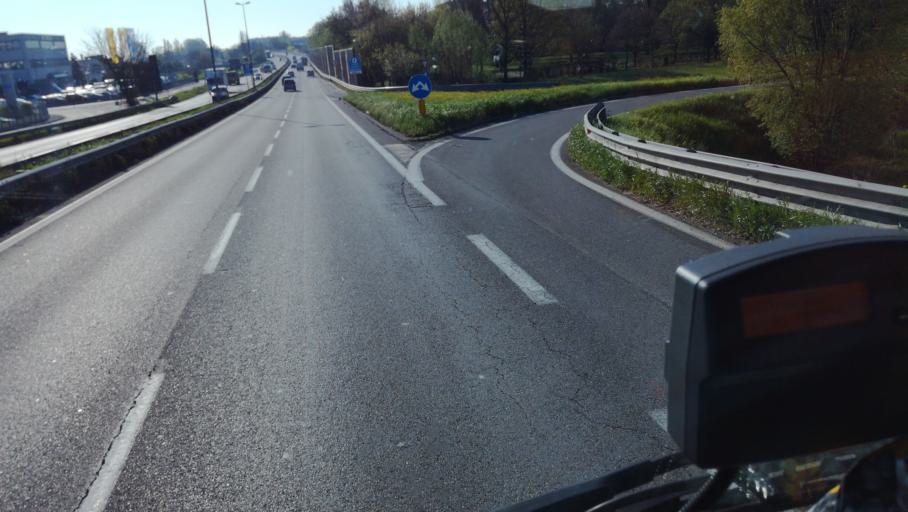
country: IT
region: Emilia-Romagna
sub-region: Provincia di Modena
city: Modena
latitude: 44.6633
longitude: 10.9398
